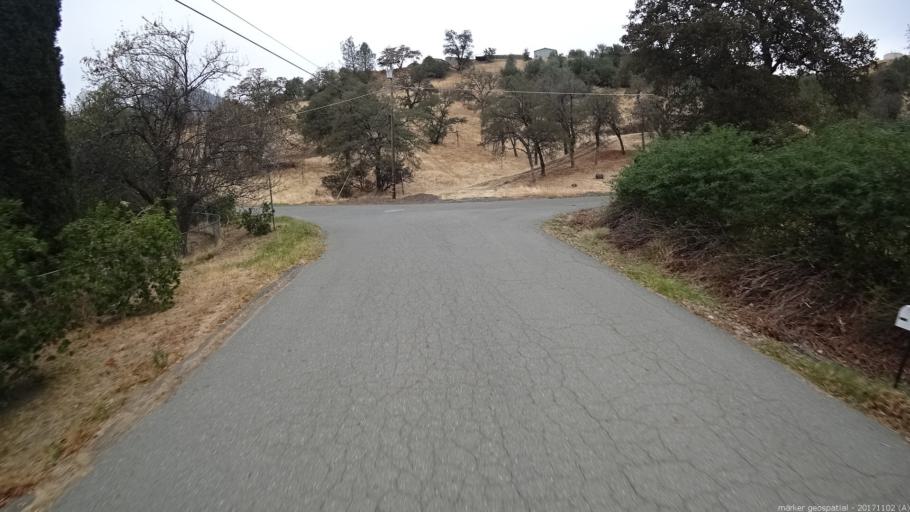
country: US
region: California
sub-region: Shasta County
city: Bella Vista
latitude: 40.7198
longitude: -122.2339
